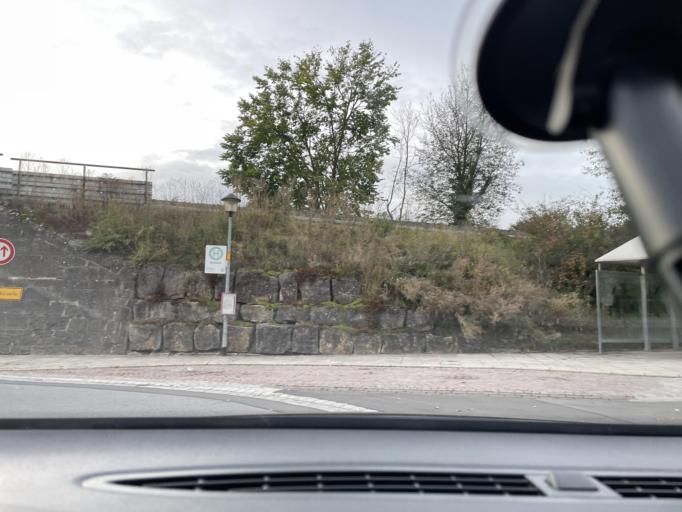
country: DE
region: Bavaria
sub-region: Regierungsbezirk Unterfranken
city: Salz
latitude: 50.3153
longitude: 10.2222
